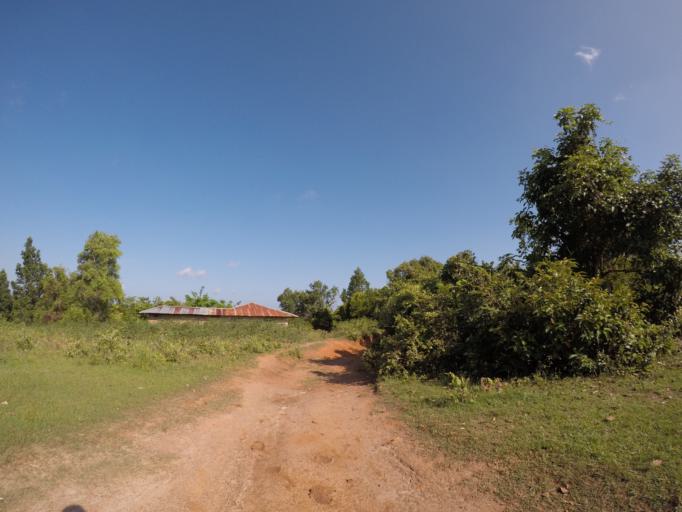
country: TZ
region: Pemba South
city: Mtambile
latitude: -5.3901
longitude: 39.7302
